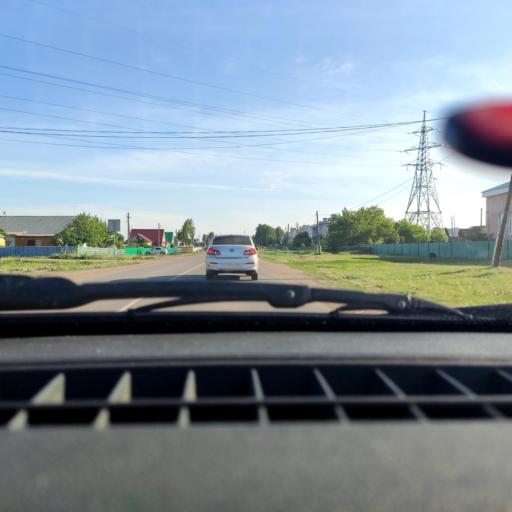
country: RU
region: Bashkortostan
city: Avdon
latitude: 54.4204
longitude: 55.8123
